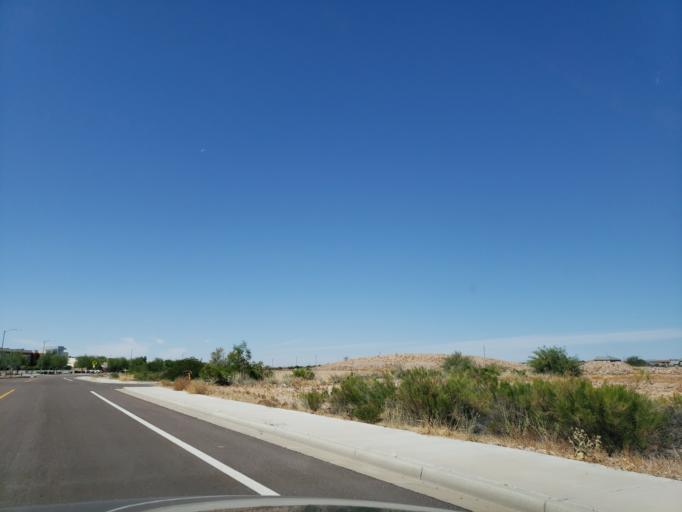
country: US
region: Arizona
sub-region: Maricopa County
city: Sun City West
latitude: 33.6790
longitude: -112.2660
